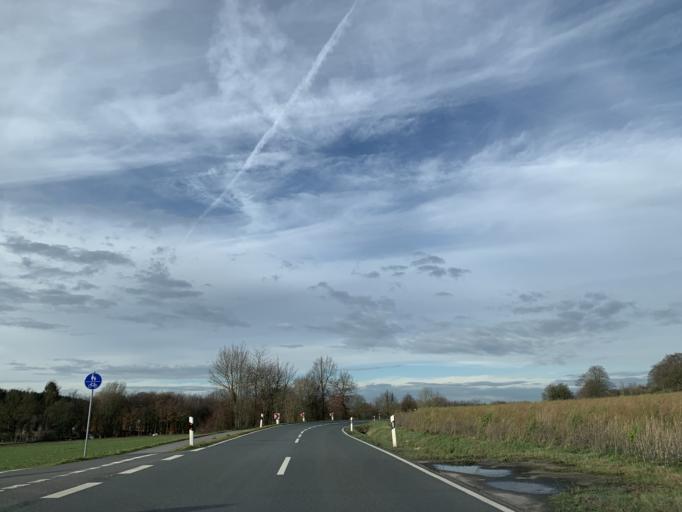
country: DE
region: North Rhine-Westphalia
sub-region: Regierungsbezirk Munster
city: Billerbeck
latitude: 51.9636
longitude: 7.3100
